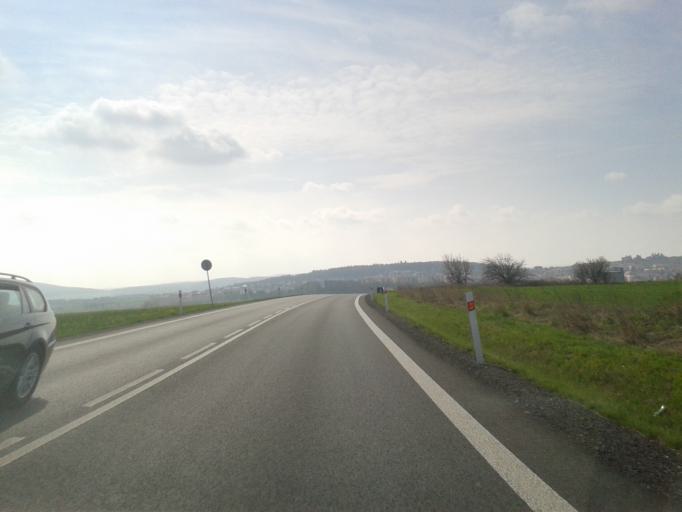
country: CZ
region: Central Bohemia
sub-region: Okres Beroun
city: Horovice
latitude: 49.8526
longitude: 13.9079
